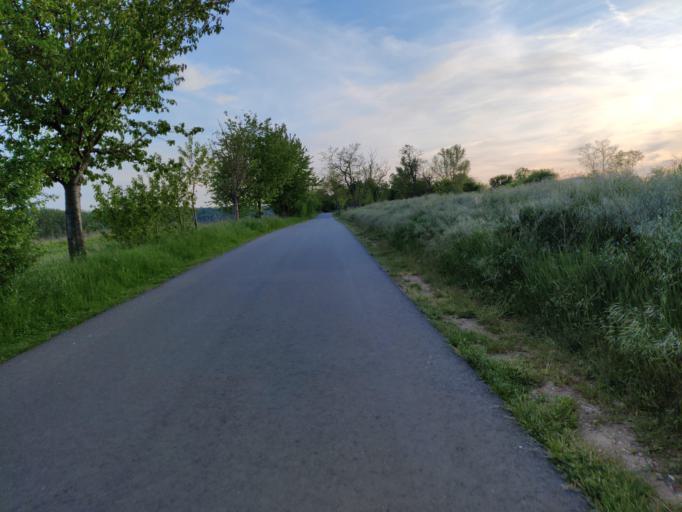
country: DE
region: Saxony-Anhalt
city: Karsdorf
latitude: 51.2485
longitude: 11.6479
